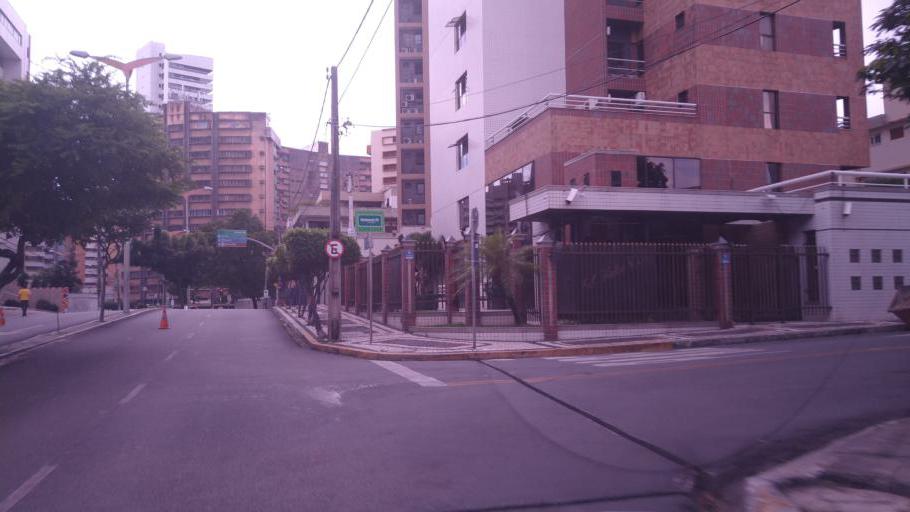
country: BR
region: Ceara
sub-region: Fortaleza
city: Fortaleza
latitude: -3.7300
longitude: -38.4909
